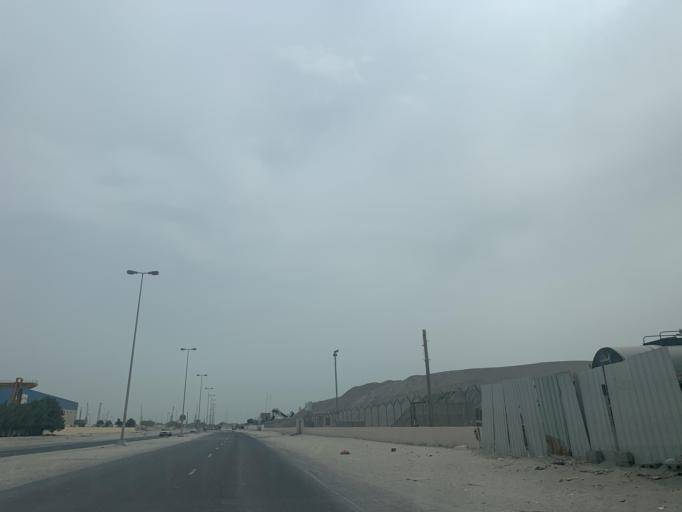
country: BH
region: Muharraq
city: Al Hadd
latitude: 26.2072
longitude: 50.6592
